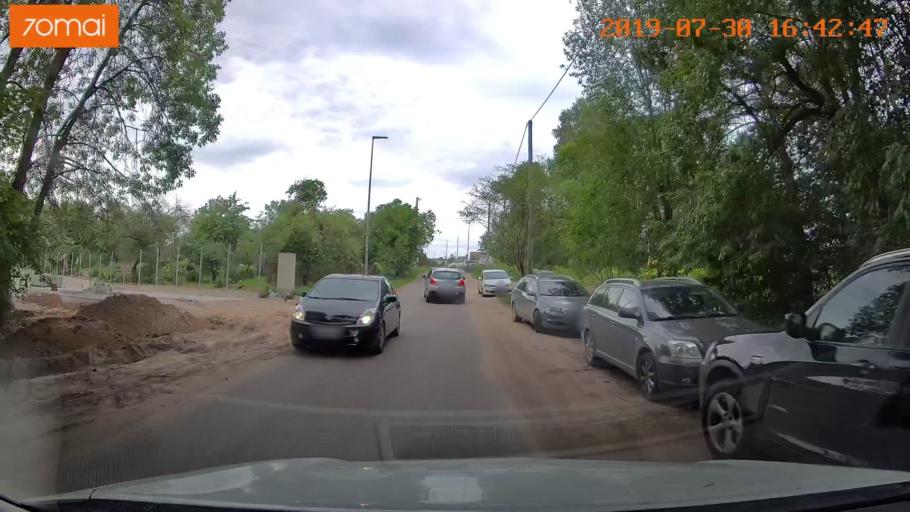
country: LT
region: Vilnius County
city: Rasos
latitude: 54.7174
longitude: 25.3515
